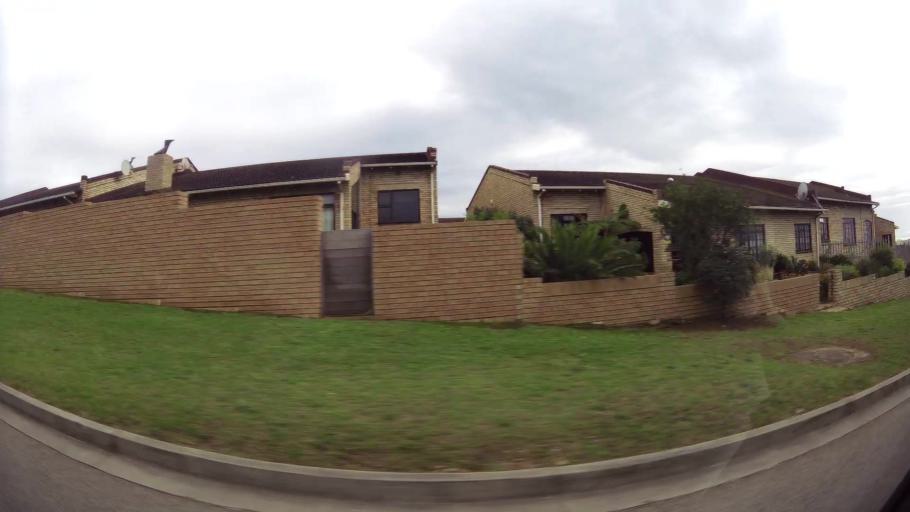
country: ZA
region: Eastern Cape
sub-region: Nelson Mandela Bay Metropolitan Municipality
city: Port Elizabeth
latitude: -33.9686
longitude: 25.6265
